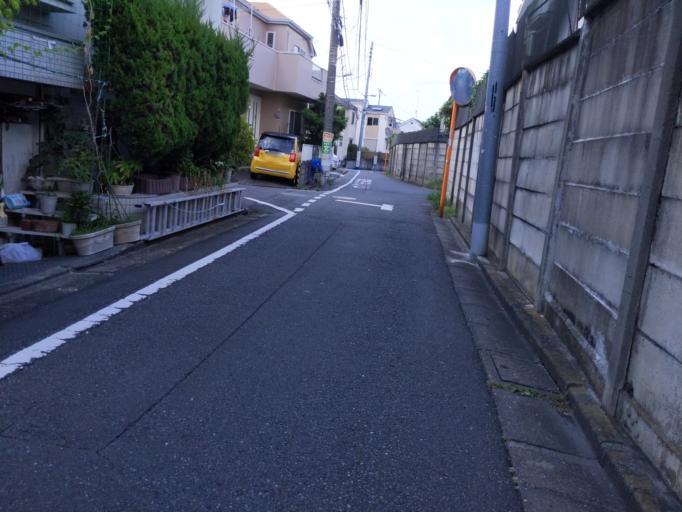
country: JP
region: Saitama
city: Wako
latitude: 35.7441
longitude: 139.6419
